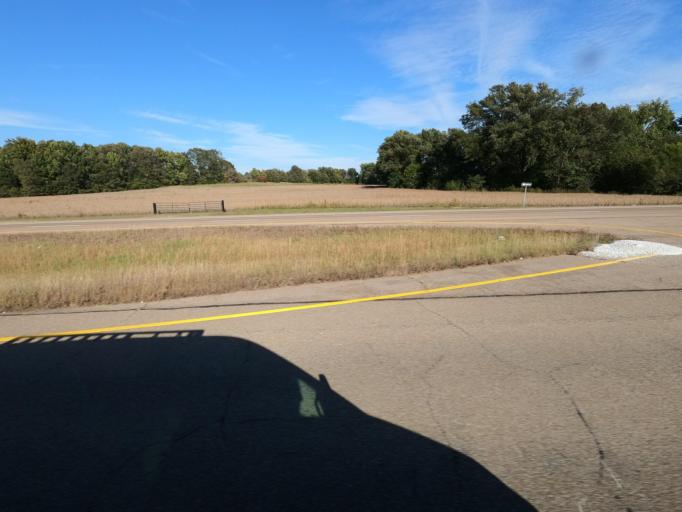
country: US
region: Tennessee
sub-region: Crockett County
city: Alamo
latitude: 35.8417
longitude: -89.1900
